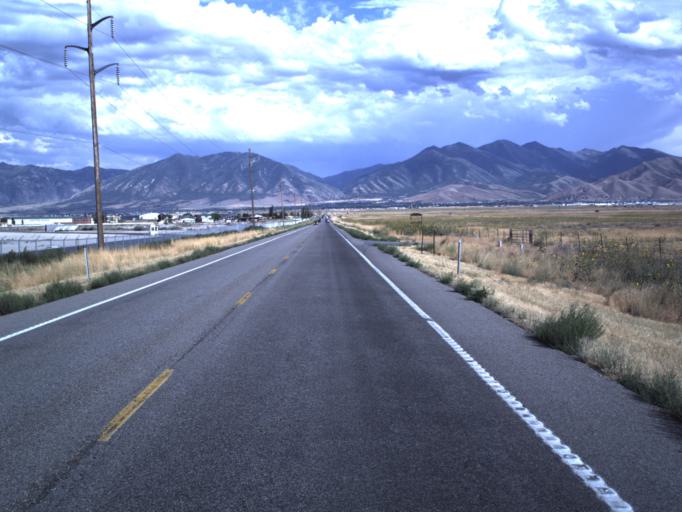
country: US
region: Utah
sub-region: Tooele County
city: Grantsville
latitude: 40.5759
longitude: -112.3878
